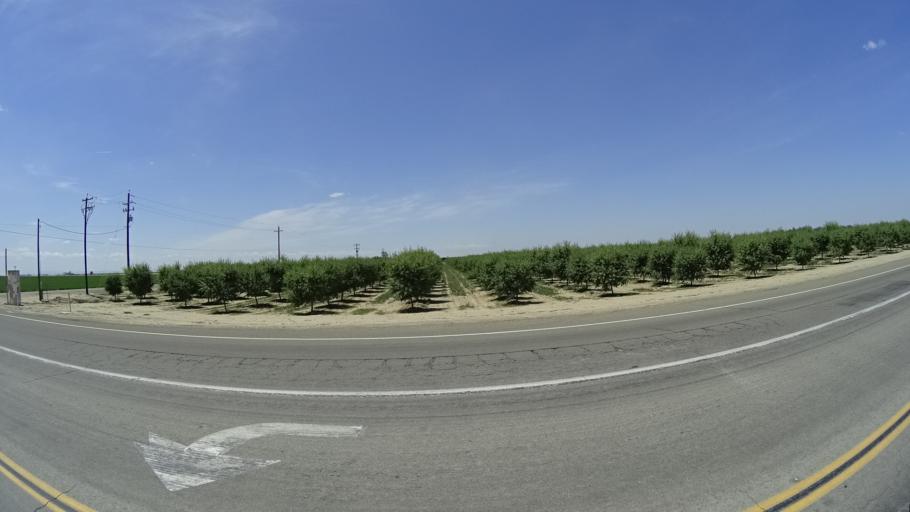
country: US
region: California
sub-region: Kings County
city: Home Garden
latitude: 36.2697
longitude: -119.6549
